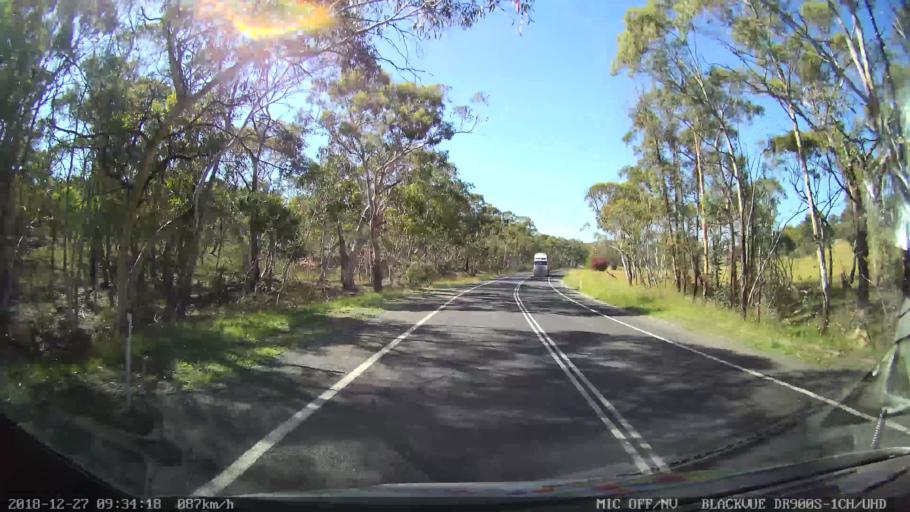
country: AU
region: New South Wales
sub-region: Lithgow
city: Portland
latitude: -33.2243
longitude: 150.0275
